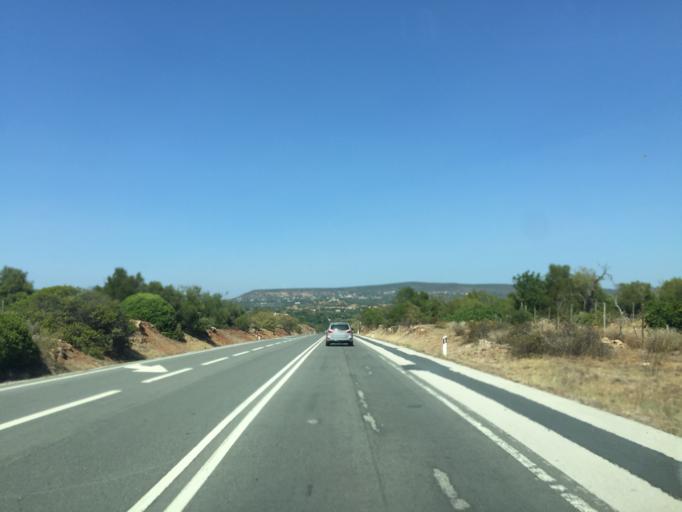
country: PT
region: Faro
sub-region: Silves
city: Sao Bartolomeu de Messines
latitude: 37.2013
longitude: -8.2606
